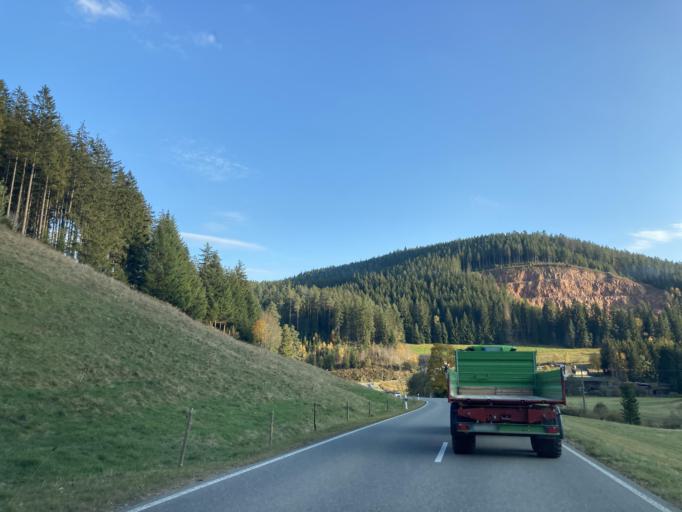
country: DE
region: Baden-Wuerttemberg
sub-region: Freiburg Region
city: Eisenbach
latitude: 47.9955
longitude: 8.3102
